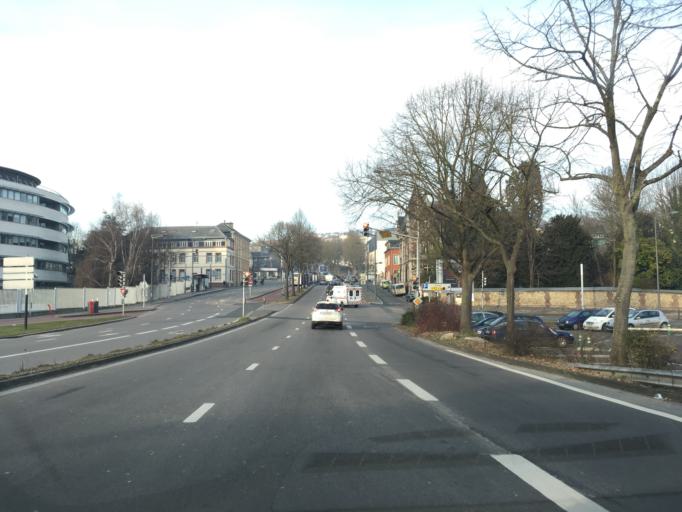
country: FR
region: Haute-Normandie
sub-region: Departement de la Seine-Maritime
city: Rouen
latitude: 49.4403
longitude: 1.1129
